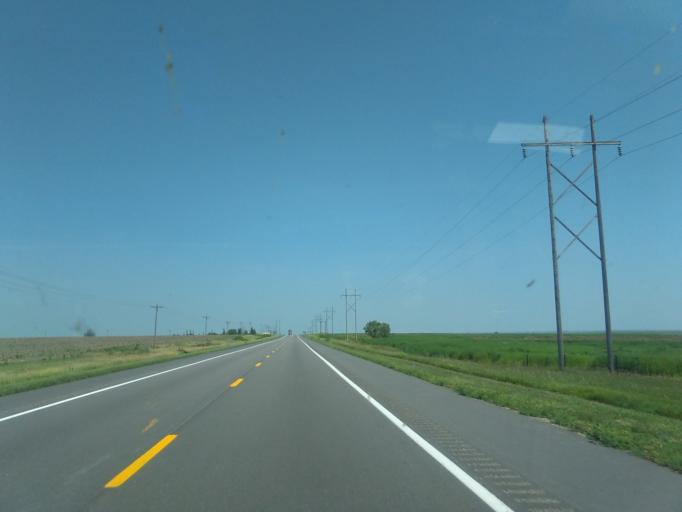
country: US
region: Nebraska
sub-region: Red Willow County
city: McCook
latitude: 40.2751
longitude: -100.6499
